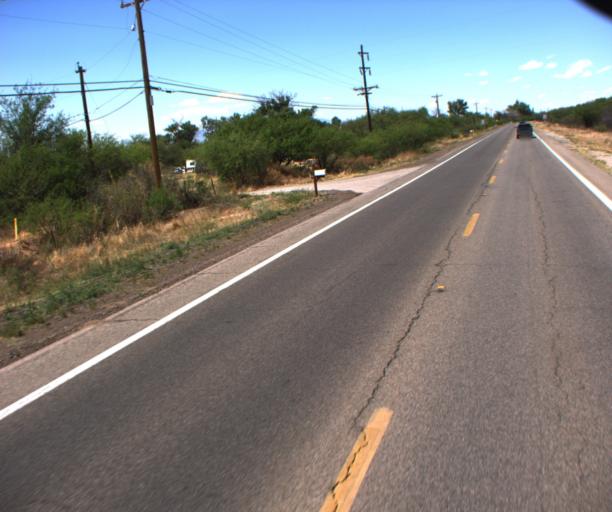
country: US
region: Arizona
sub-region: Cochise County
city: Saint David
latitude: 31.8776
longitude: -110.2112
